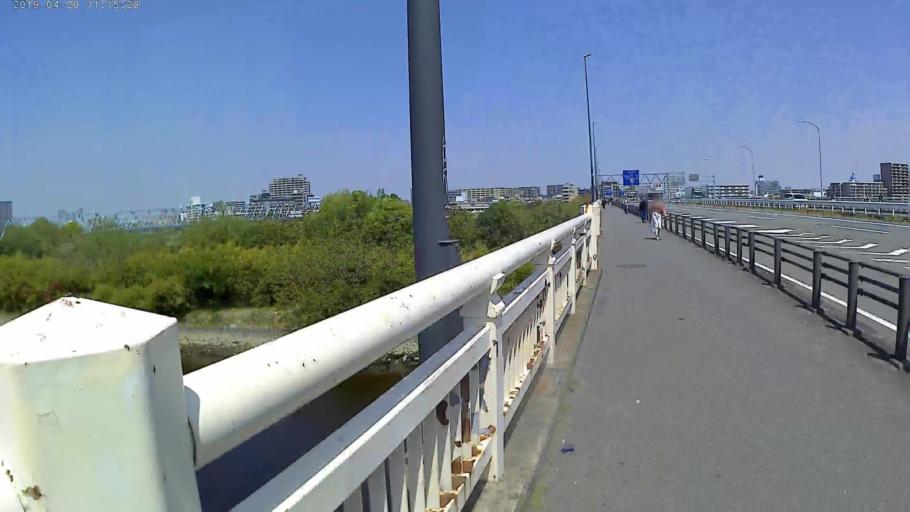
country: JP
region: Kanagawa
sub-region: Kawasaki-shi
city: Kawasaki
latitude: 35.5365
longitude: 139.7080
